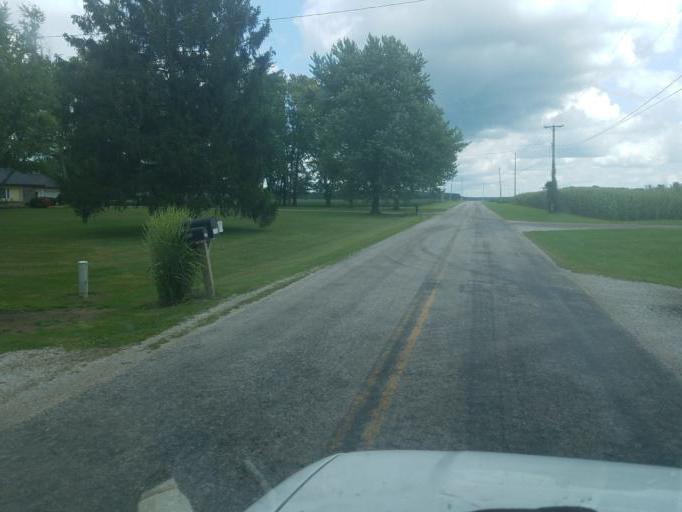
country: US
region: Ohio
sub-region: Ashtabula County
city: Roaming Shores
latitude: 41.5884
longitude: -80.7511
